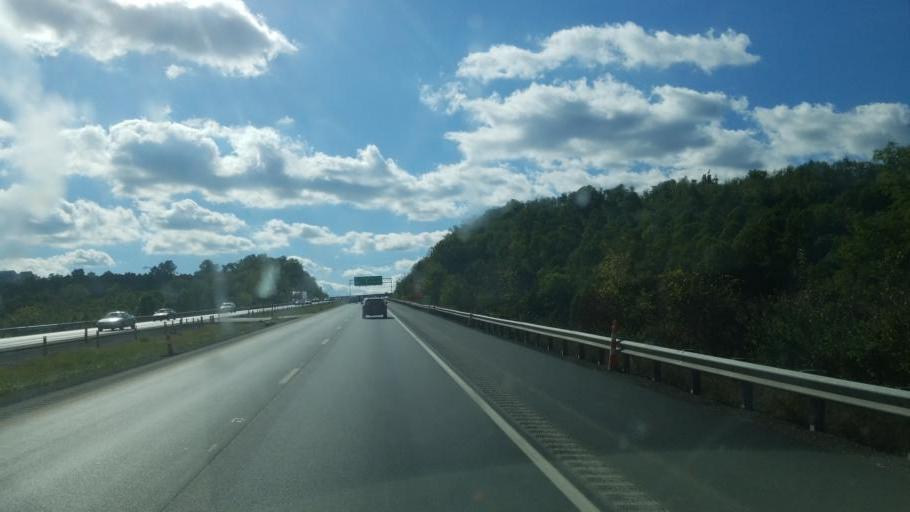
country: US
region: West Virginia
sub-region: Monongalia County
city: Morgantown
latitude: 39.5872
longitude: -79.9447
